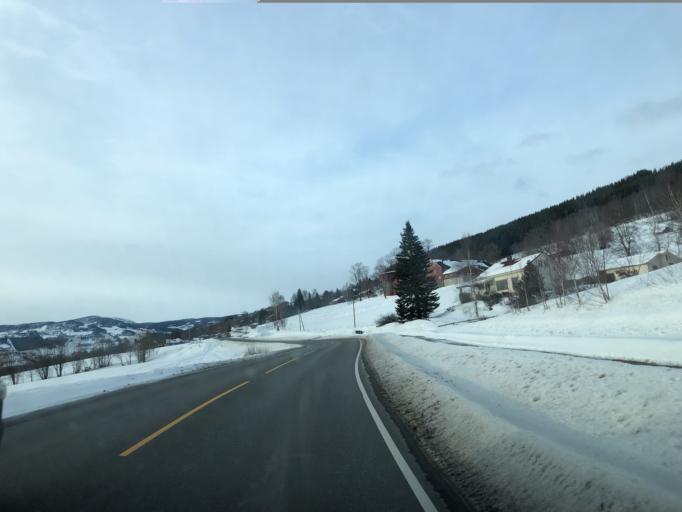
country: NO
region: Oppland
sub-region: Gausdal
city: Segalstad bru
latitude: 61.2422
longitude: 10.1978
